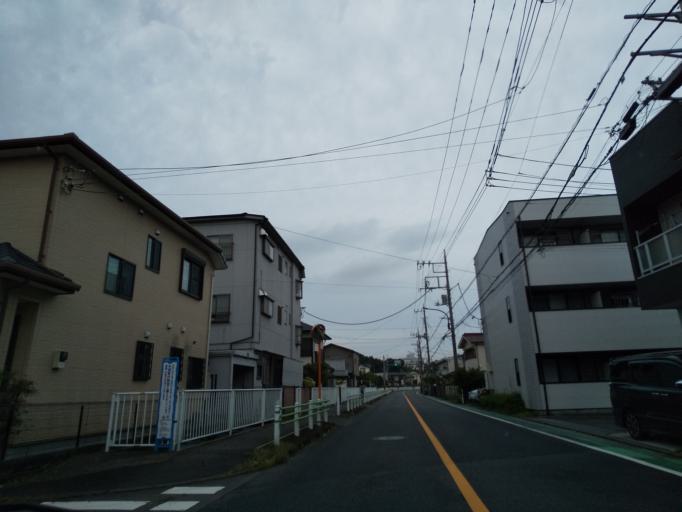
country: JP
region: Tokyo
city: Hino
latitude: 35.6835
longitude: 139.3838
